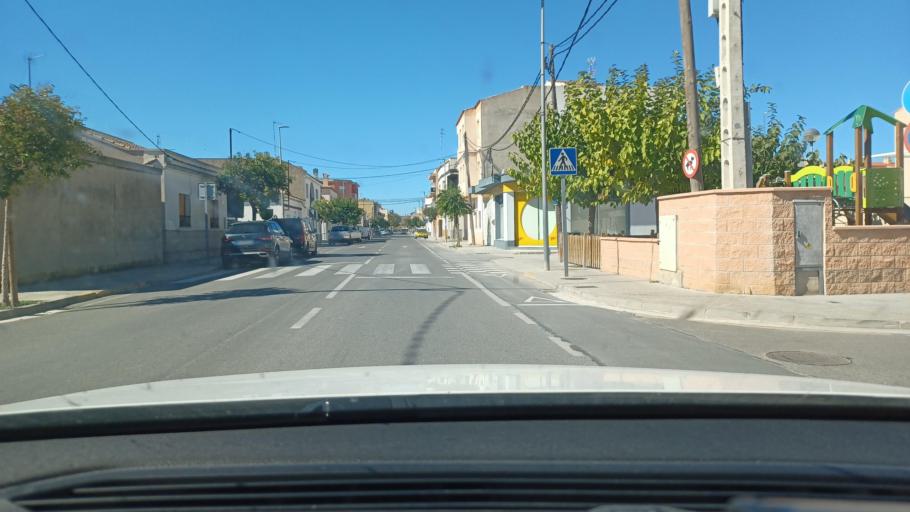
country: ES
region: Catalonia
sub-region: Provincia de Tarragona
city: Deltebre
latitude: 40.7201
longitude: 0.7339
